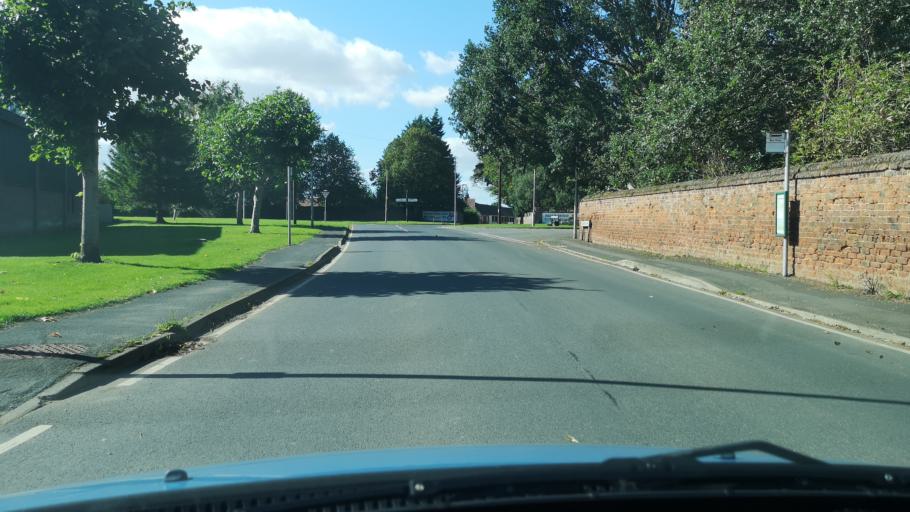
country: GB
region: England
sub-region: North Lincolnshire
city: Eastoft
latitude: 53.6360
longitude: -0.7834
